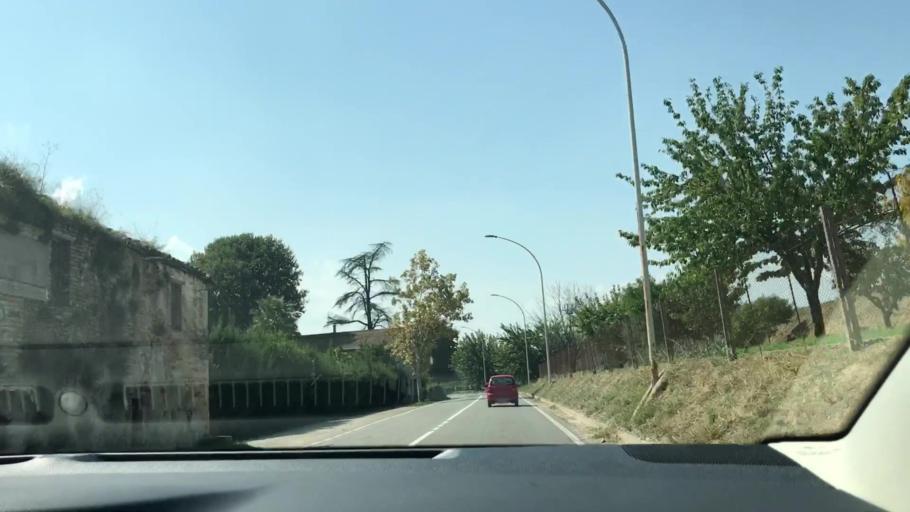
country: IT
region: The Marches
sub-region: Provincia di Ascoli Piceno
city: Centobuchi
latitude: 42.8946
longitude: 13.8383
